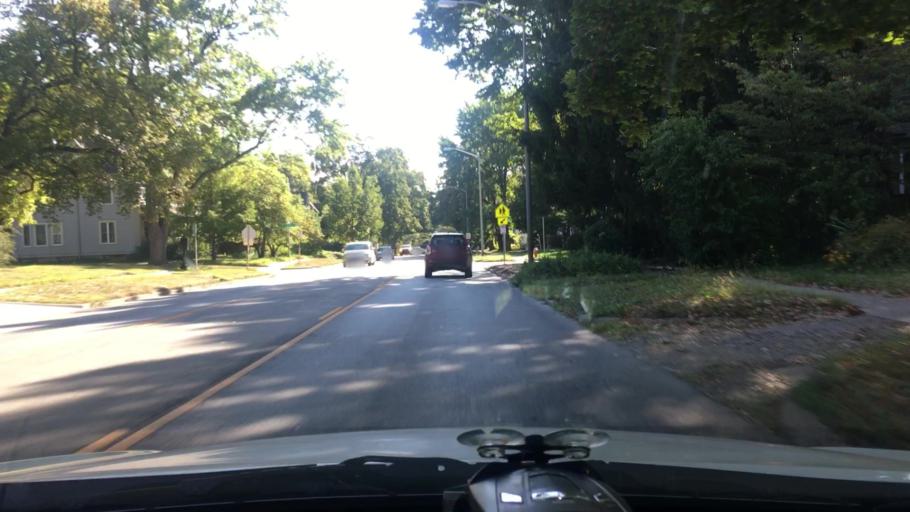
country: US
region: Illinois
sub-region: Champaign County
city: Champaign
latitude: 40.1126
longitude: -88.2549
